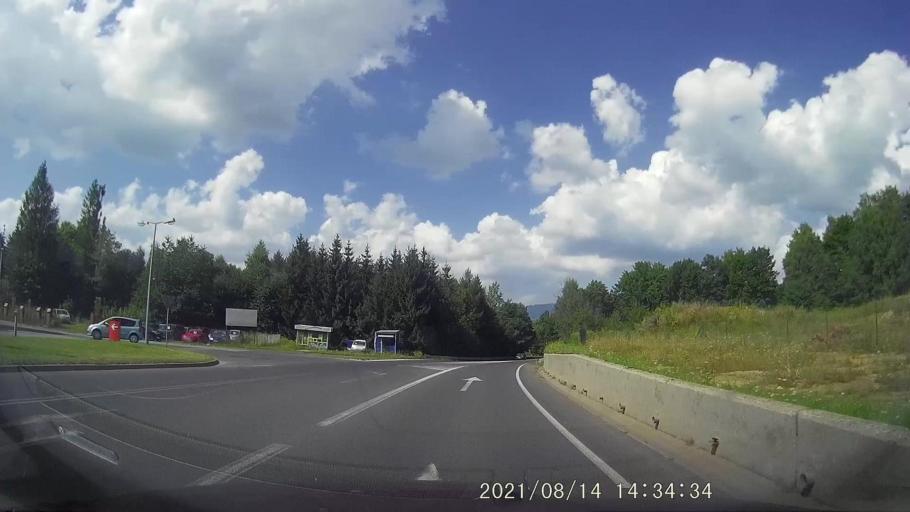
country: PL
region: Lower Silesian Voivodeship
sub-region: Powiat klodzki
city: Nowa Ruda
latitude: 50.5671
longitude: 16.5335
